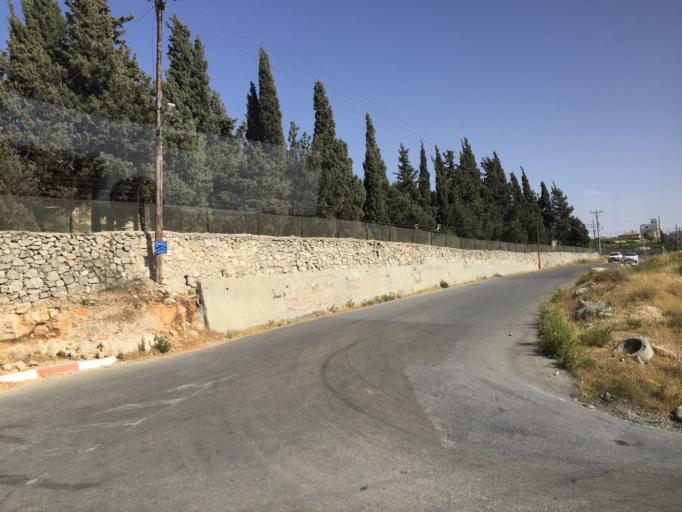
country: PS
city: Ad Dawhah
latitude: 31.7073
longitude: 35.1718
